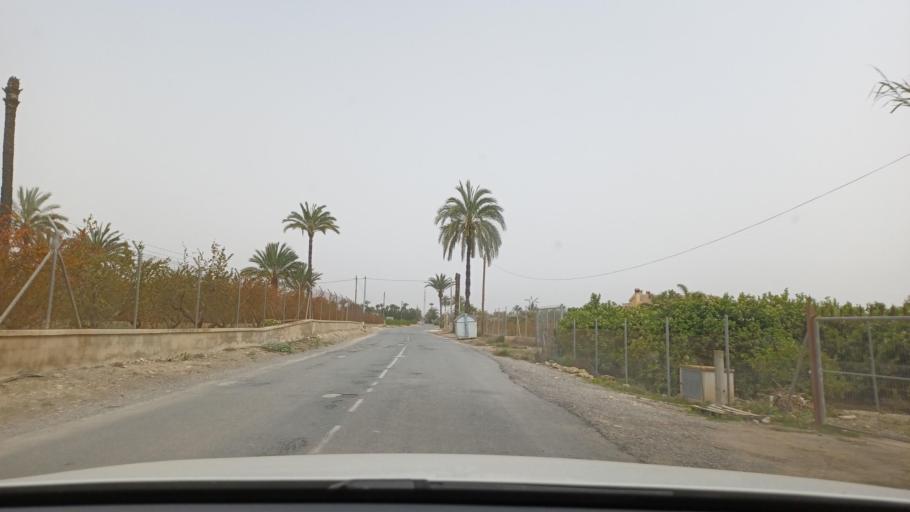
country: ES
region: Valencia
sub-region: Provincia de Alicante
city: Elche
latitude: 38.2253
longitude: -0.6948
